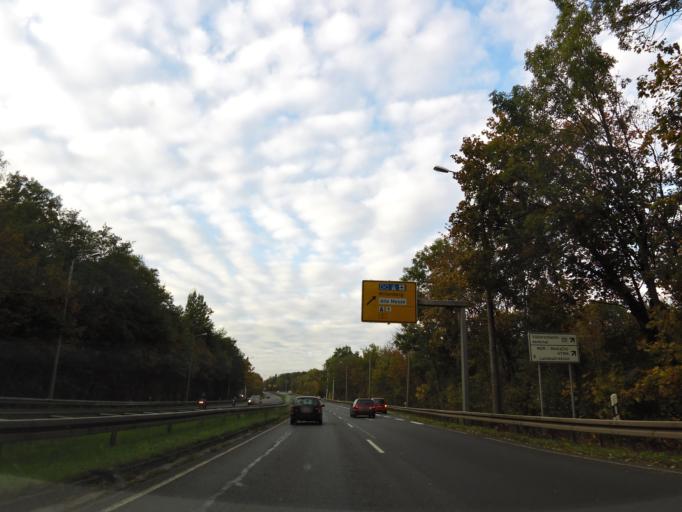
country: DE
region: Saxony
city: Leipzig
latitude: 51.3108
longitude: 12.3645
